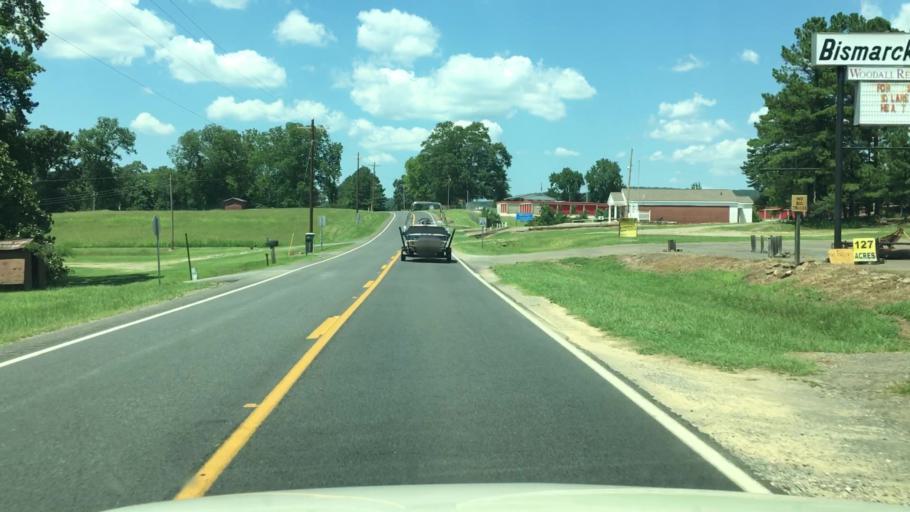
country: US
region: Arkansas
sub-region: Garland County
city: Lake Hamilton
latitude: 34.3233
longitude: -93.1730
